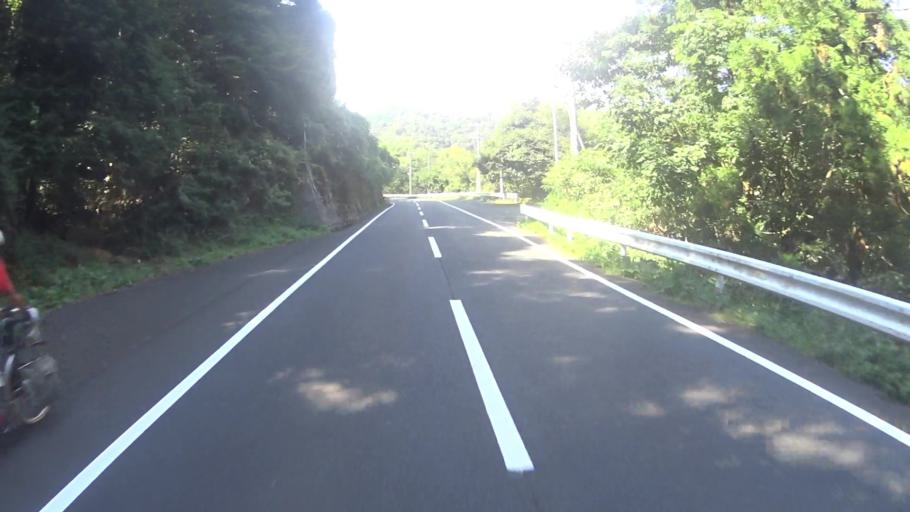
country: JP
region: Kyoto
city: Miyazu
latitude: 35.7054
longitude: 135.2817
